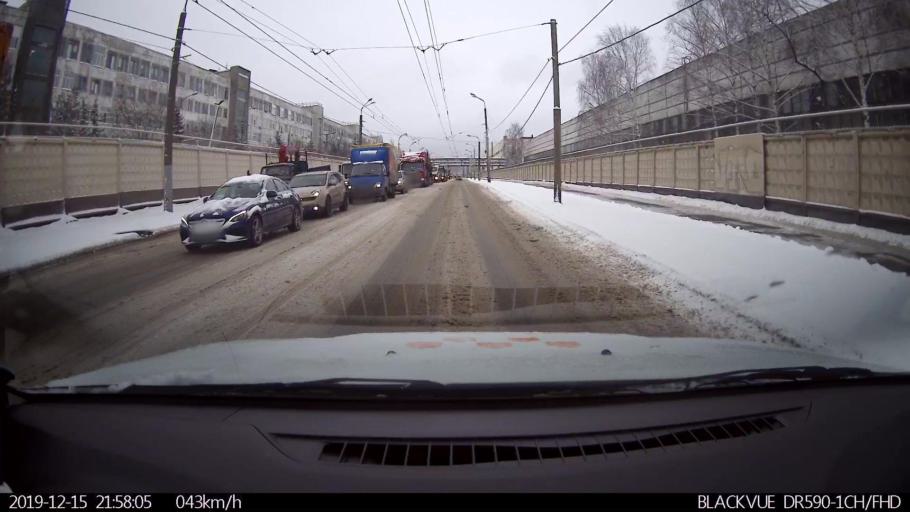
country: RU
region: Nizjnij Novgorod
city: Nizhniy Novgorod
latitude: 56.2454
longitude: 43.9075
